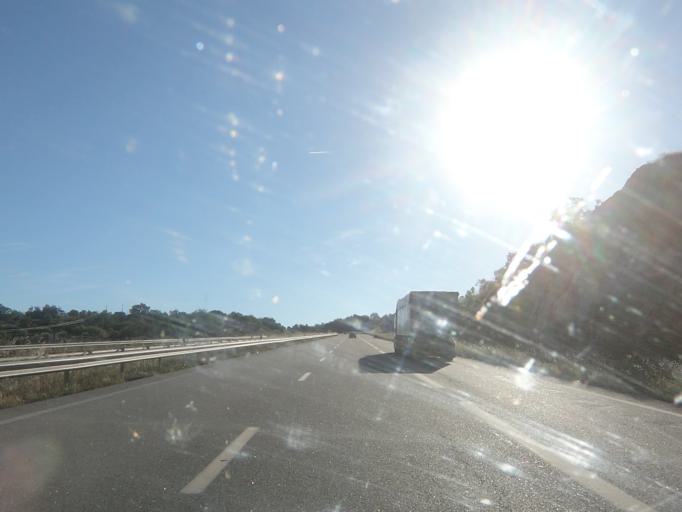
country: ES
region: Castille and Leon
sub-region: Provincia de Salamanca
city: Fuentes de Onoro
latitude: 40.6072
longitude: -6.9335
